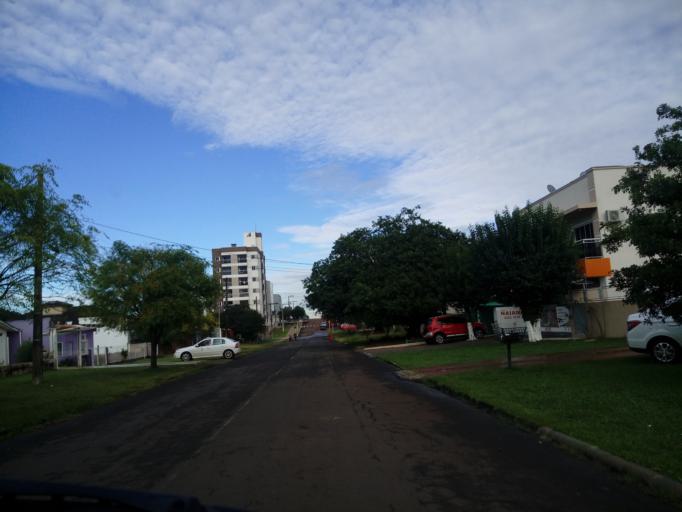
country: BR
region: Santa Catarina
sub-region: Chapeco
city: Chapeco
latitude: -27.1075
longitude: -52.6268
